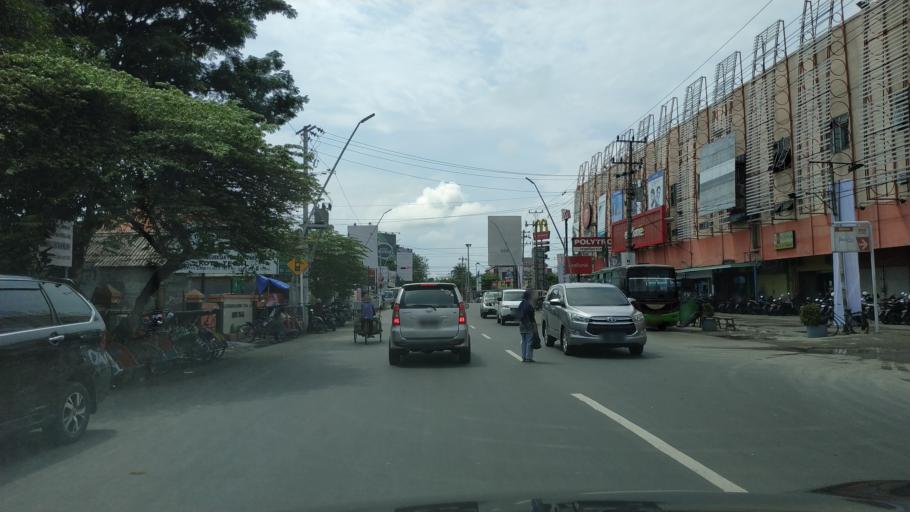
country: ID
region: Central Java
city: Tegal
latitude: -6.8704
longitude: 109.1282
